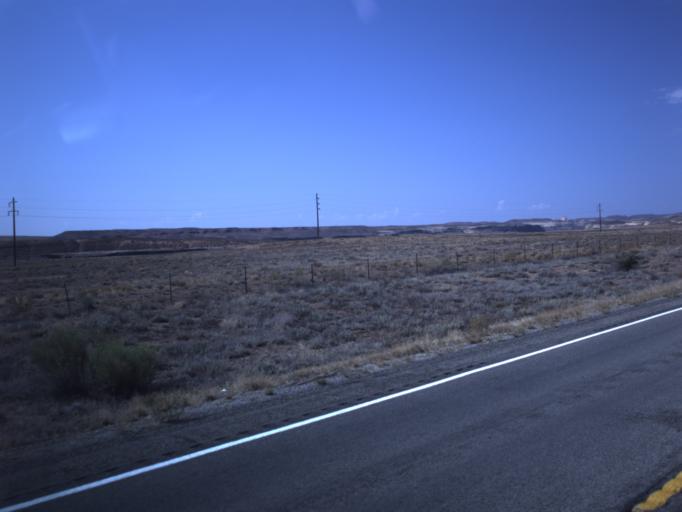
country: US
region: Utah
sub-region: San Juan County
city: Blanding
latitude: 37.2682
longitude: -109.6048
